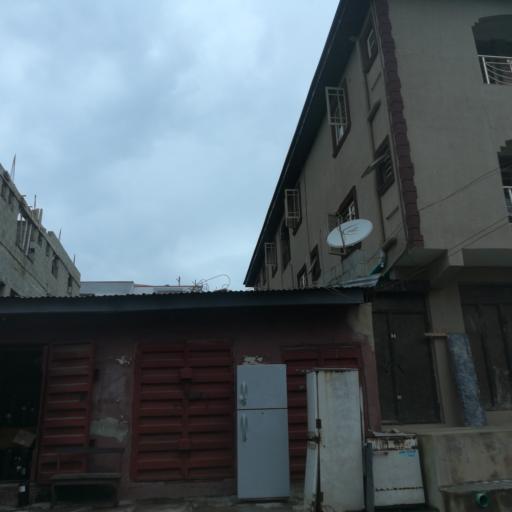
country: NG
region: Lagos
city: Makoko
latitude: 6.4915
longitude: 3.3799
